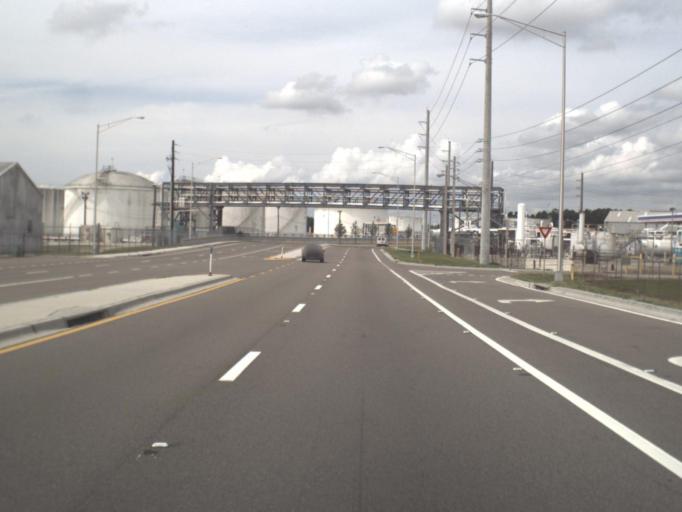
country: US
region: Florida
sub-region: Duval County
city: Jacksonville
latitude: 30.4152
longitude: -81.6036
